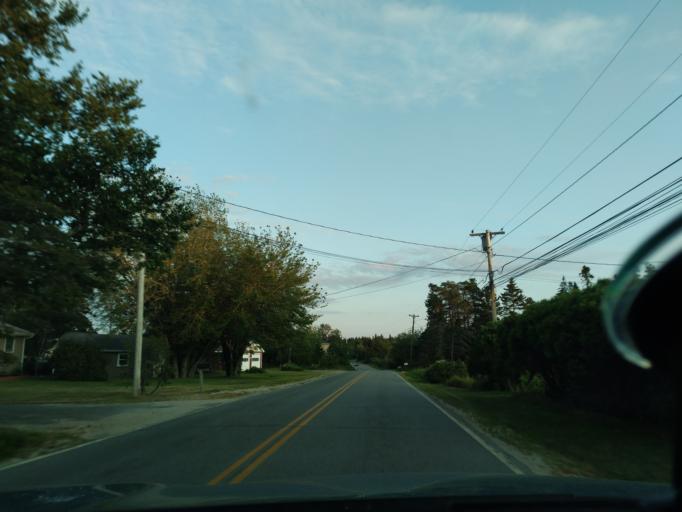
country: US
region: Maine
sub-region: Hancock County
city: Gouldsboro
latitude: 44.3749
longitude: -68.0352
